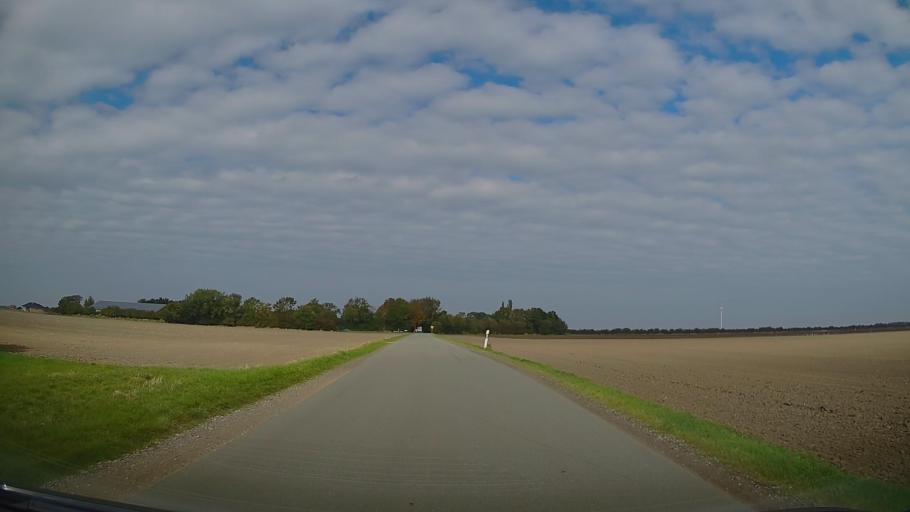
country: DE
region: Schleswig-Holstein
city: Grossenbrode
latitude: 54.5170
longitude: 11.0544
